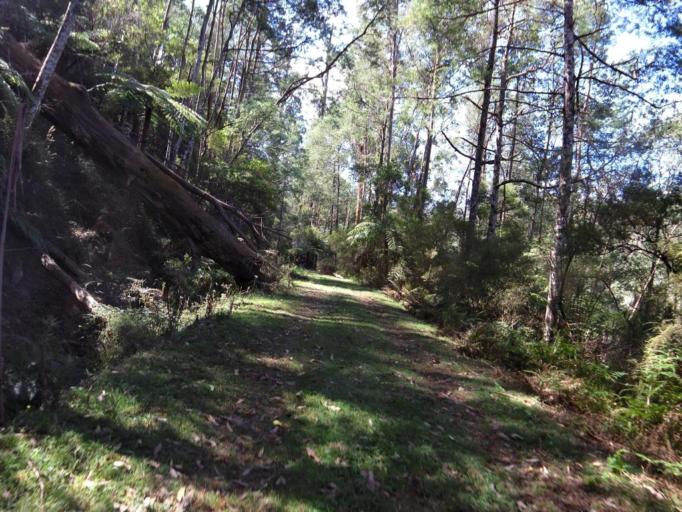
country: AU
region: Victoria
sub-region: Yarra Ranges
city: Millgrove
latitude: -37.6932
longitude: 145.8030
